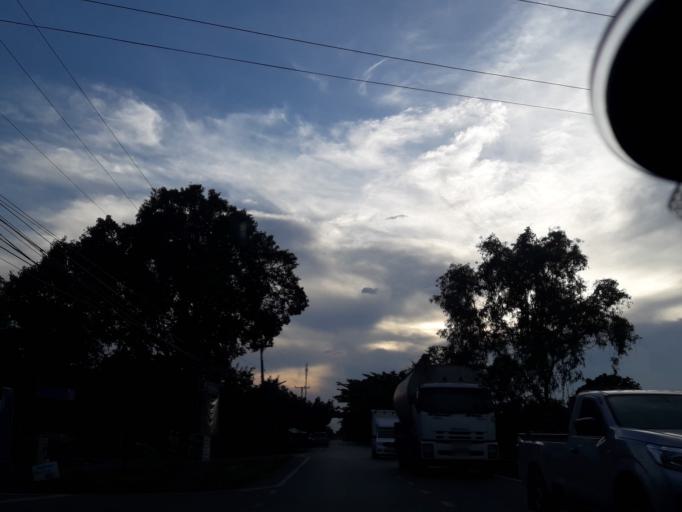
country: TH
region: Sara Buri
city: Nong Khae
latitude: 14.2650
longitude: 100.8689
